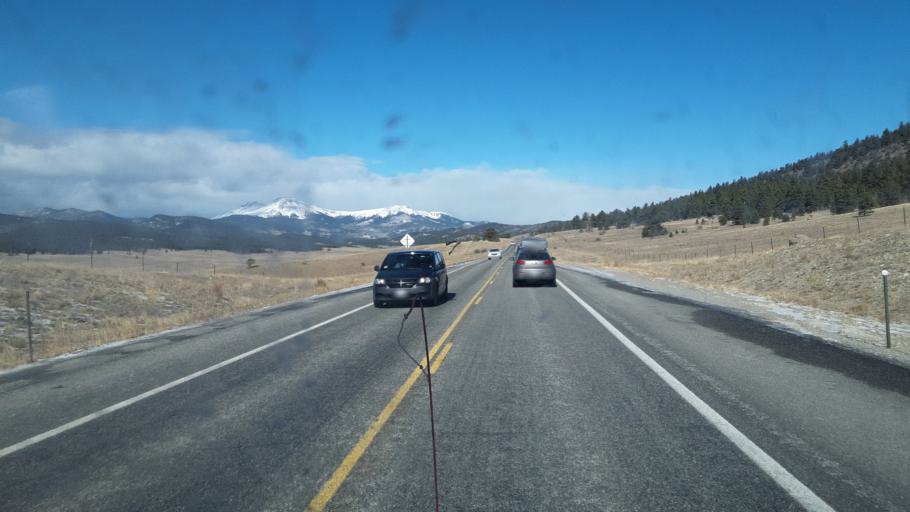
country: US
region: Colorado
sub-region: Chaffee County
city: Buena Vista
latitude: 38.8756
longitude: -105.9853
